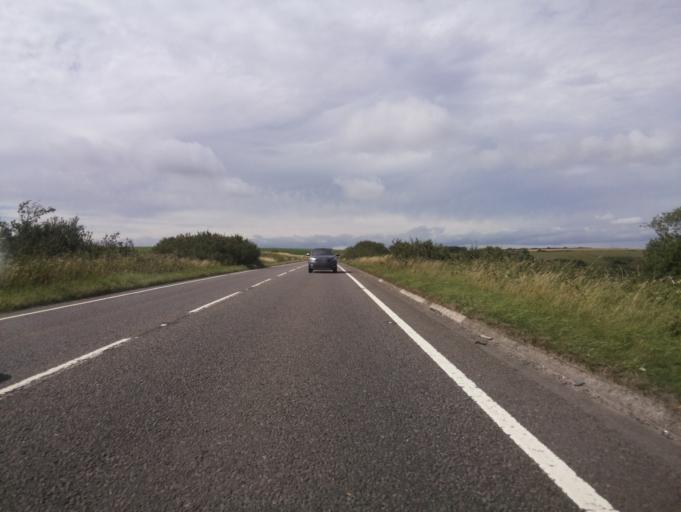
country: GB
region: England
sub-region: Dorset
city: Dorchester
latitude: 50.7903
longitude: -2.5458
